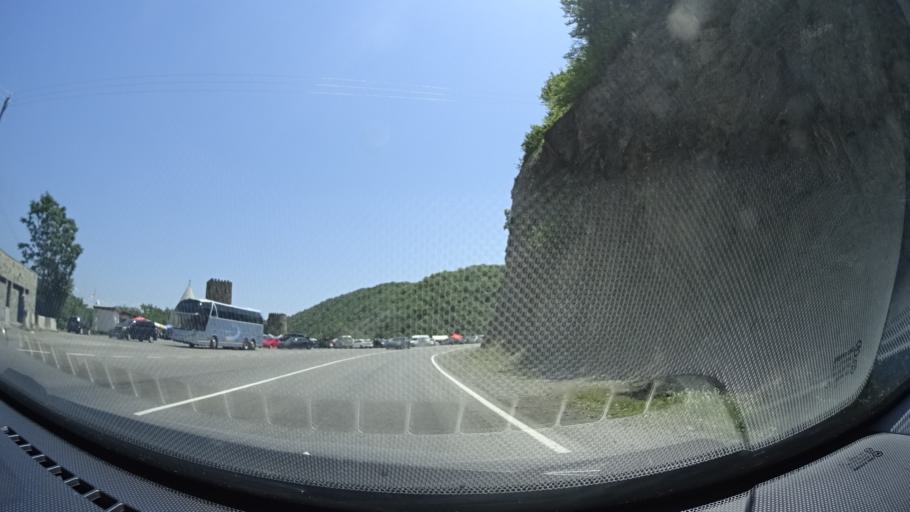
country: GE
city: Zhinvali
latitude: 42.1642
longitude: 44.7012
